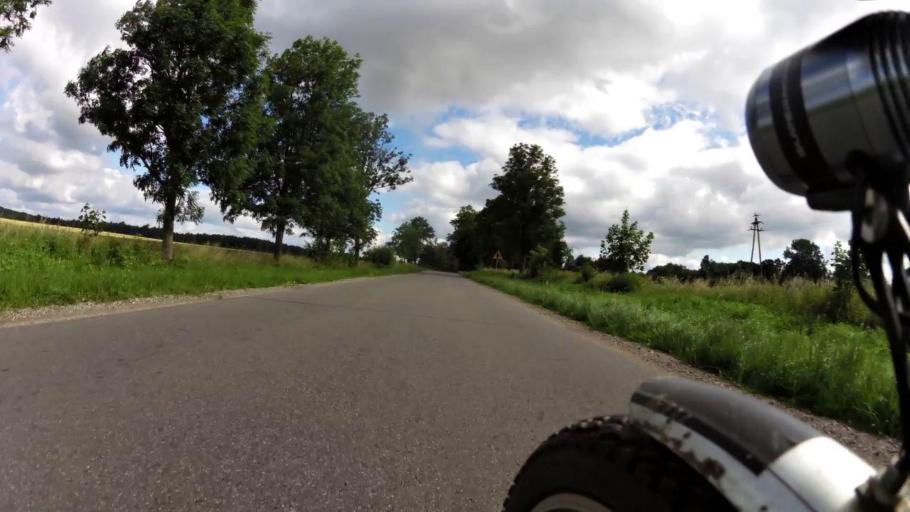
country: PL
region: West Pomeranian Voivodeship
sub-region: Powiat swidwinski
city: Rabino
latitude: 53.7940
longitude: 15.9059
